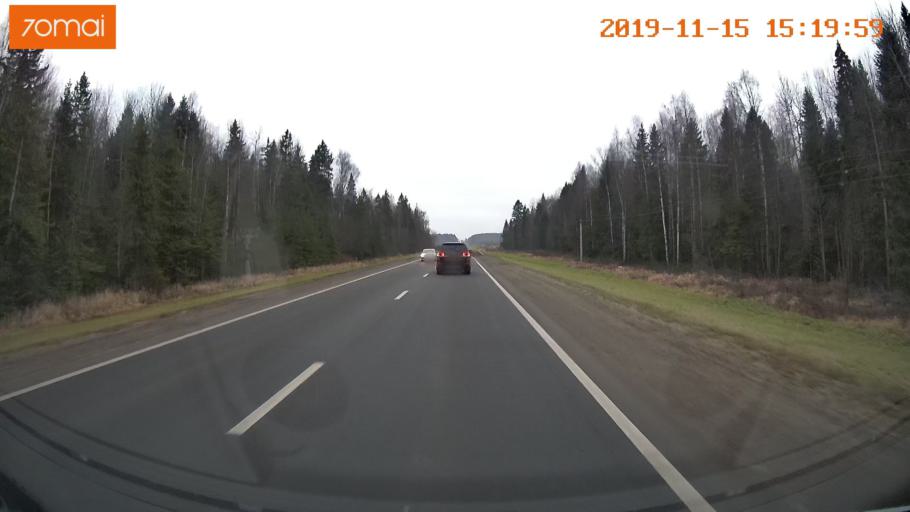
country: RU
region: Jaroslavl
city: Danilov
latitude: 58.2285
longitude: 40.1691
